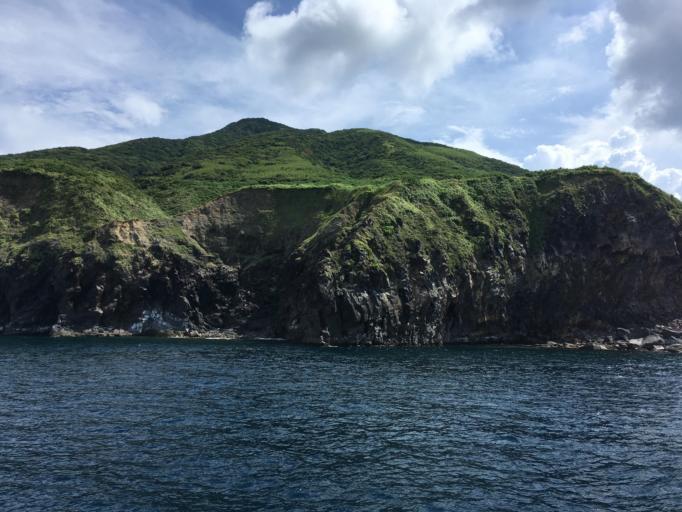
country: TW
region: Taiwan
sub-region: Yilan
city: Yilan
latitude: 24.8519
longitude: 121.9515
